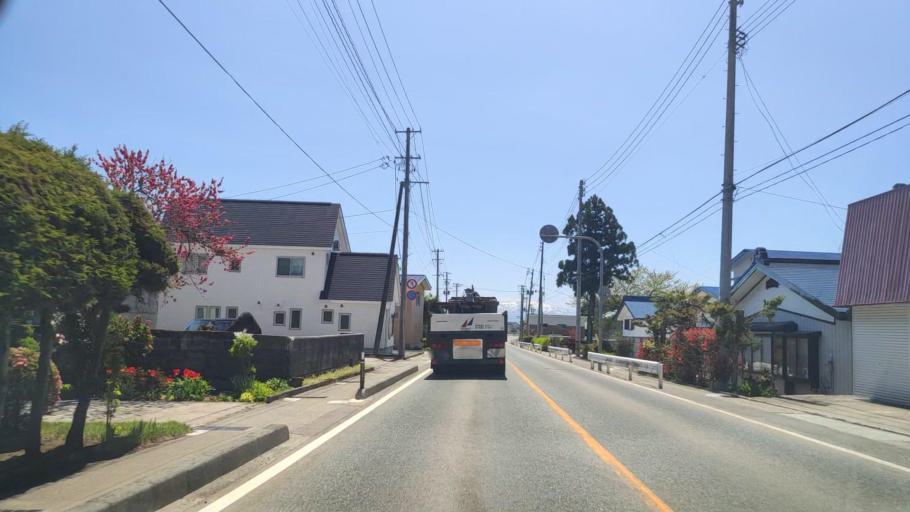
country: JP
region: Yamagata
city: Shinjo
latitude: 38.8017
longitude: 140.3202
